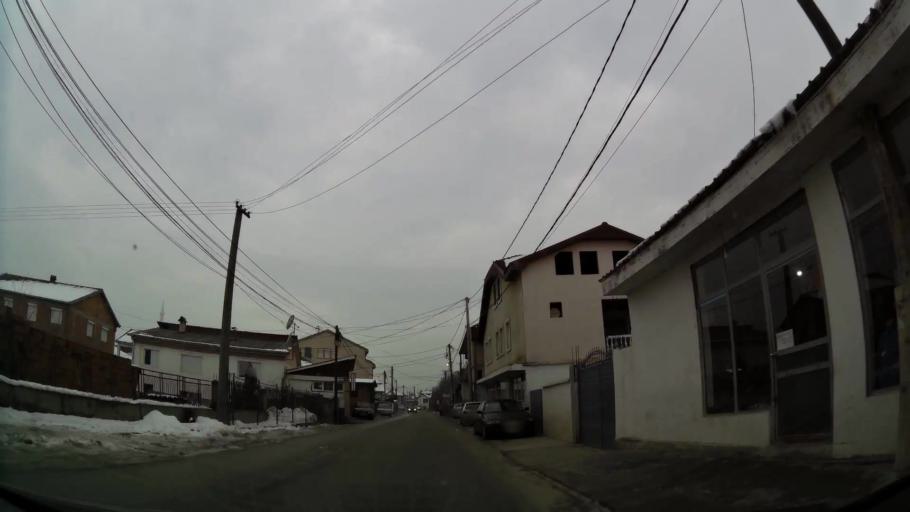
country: MK
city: Kondovo
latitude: 42.0102
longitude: 21.3206
